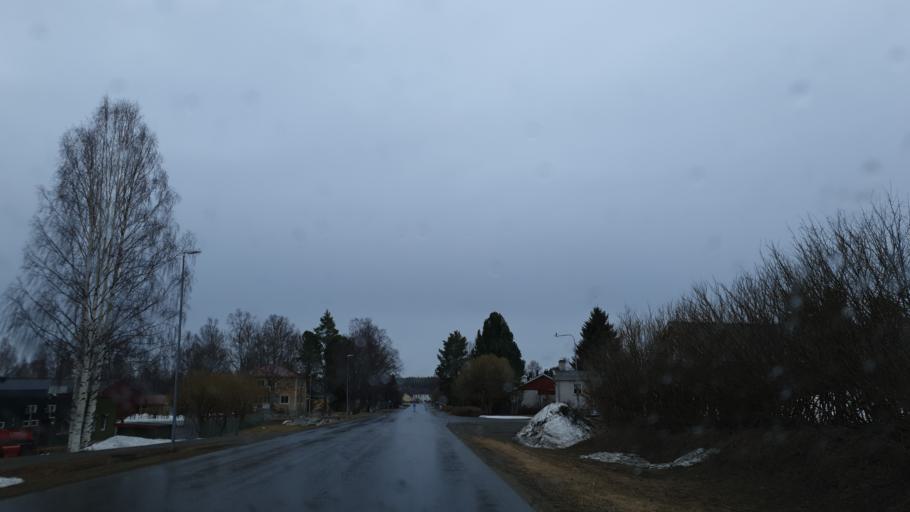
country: SE
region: Vaesterbotten
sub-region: Skelleftea Kommun
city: Kage
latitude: 64.8401
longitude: 20.9852
